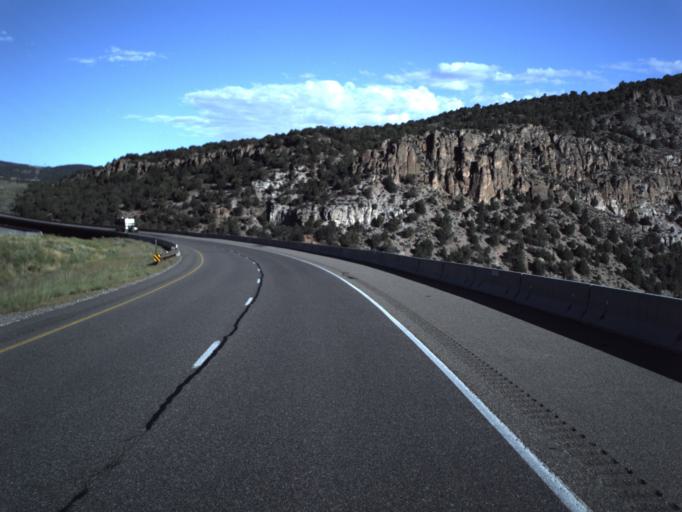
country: US
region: Utah
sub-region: Sevier County
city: Monroe
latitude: 38.5625
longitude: -112.4281
